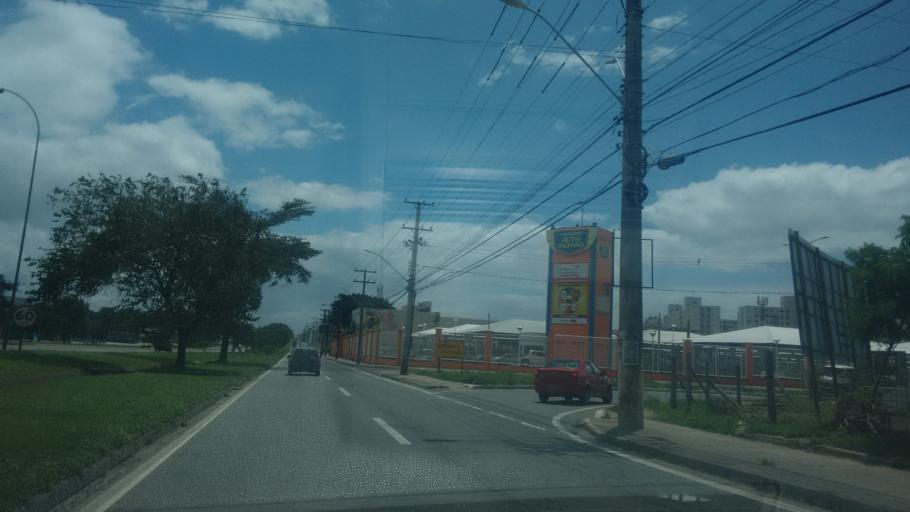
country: BR
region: Espirito Santo
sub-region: Serra
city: Serra
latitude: -20.2025
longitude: -40.2689
